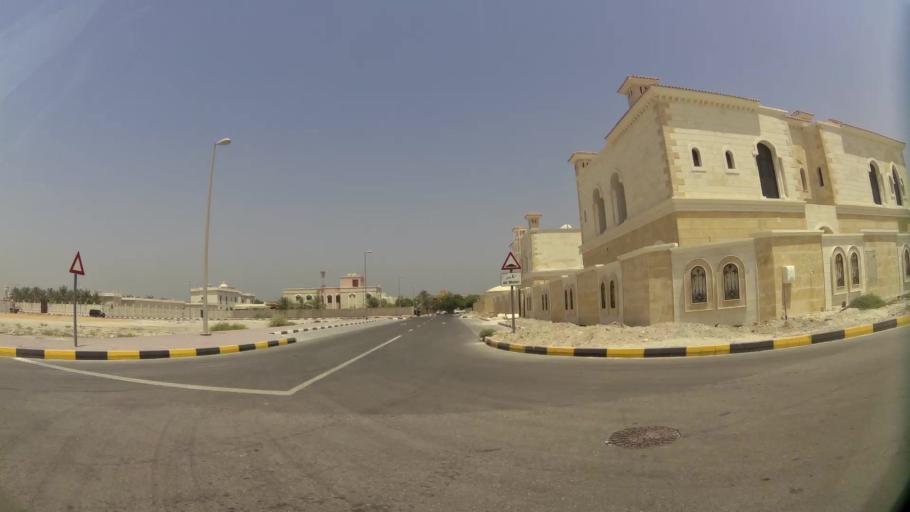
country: AE
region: Ash Shariqah
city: Sharjah
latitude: 25.3429
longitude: 55.3727
